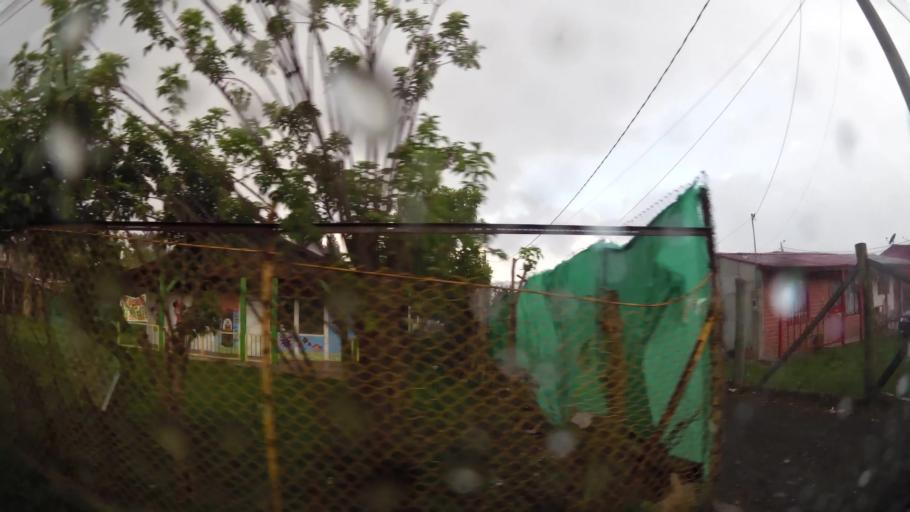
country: CO
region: Cundinamarca
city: Chia
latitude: 4.8601
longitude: -74.0712
